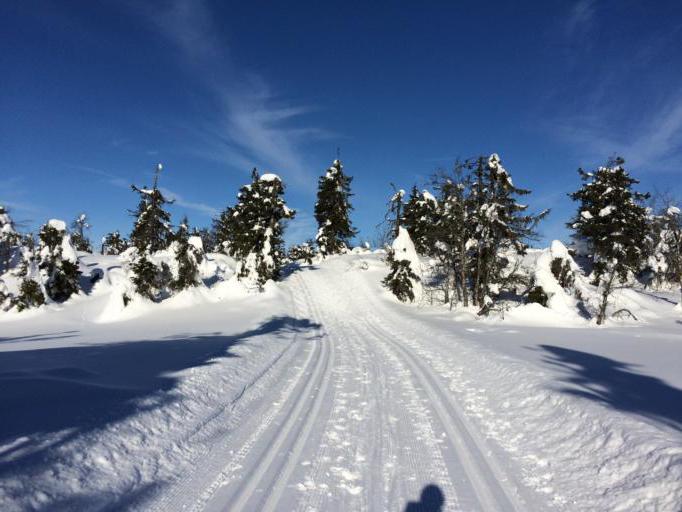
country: NO
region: Oppland
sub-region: Gausdal
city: Segalstad bru
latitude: 61.3091
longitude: 10.1031
